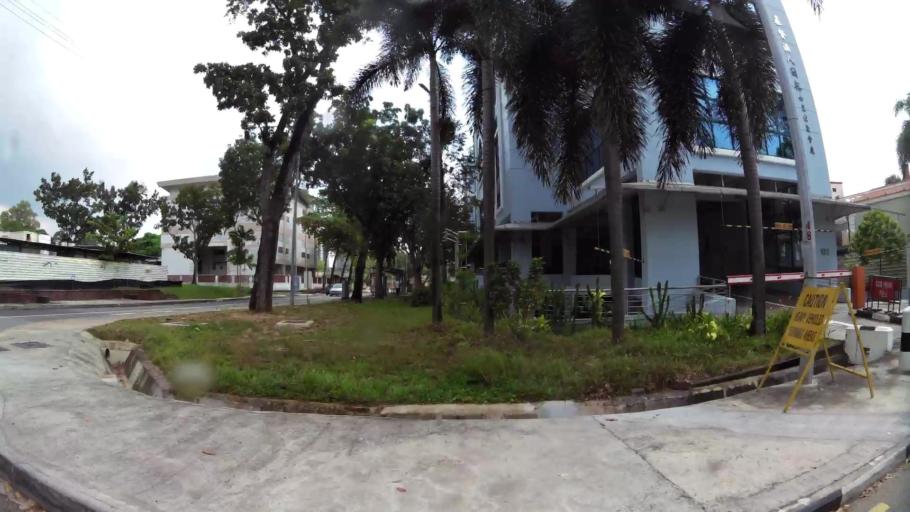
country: SG
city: Singapore
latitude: 1.2997
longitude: 103.8033
